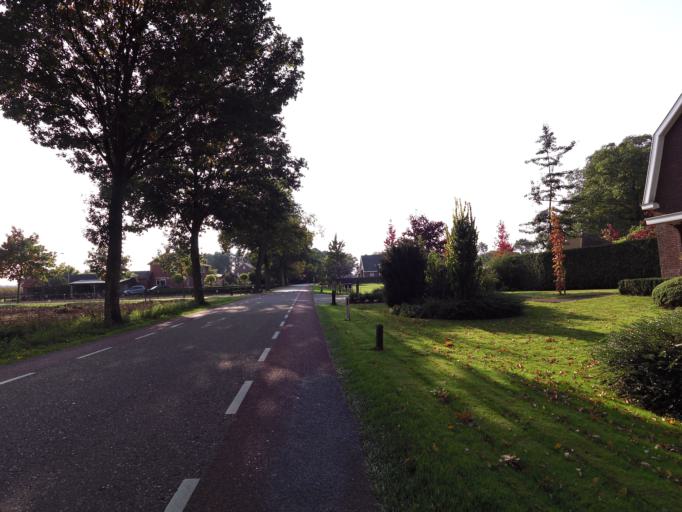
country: NL
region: Gelderland
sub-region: Gemeente Aalten
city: Aalten
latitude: 51.9101
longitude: 6.5256
